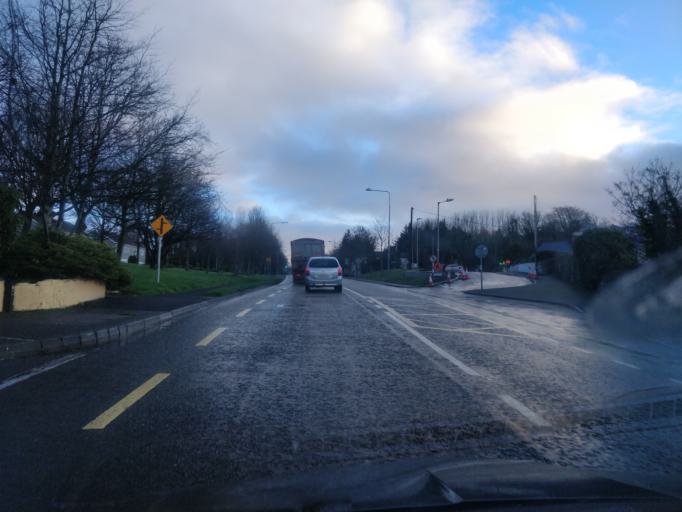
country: IE
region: Connaught
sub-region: Maigh Eo
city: Westport
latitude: 53.8026
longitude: -9.5126
